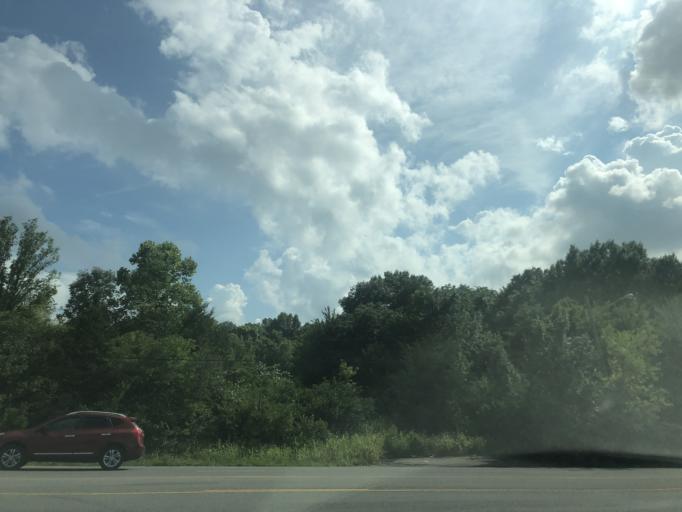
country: US
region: Tennessee
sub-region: Davidson County
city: Lakewood
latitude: 36.1573
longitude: -86.6346
